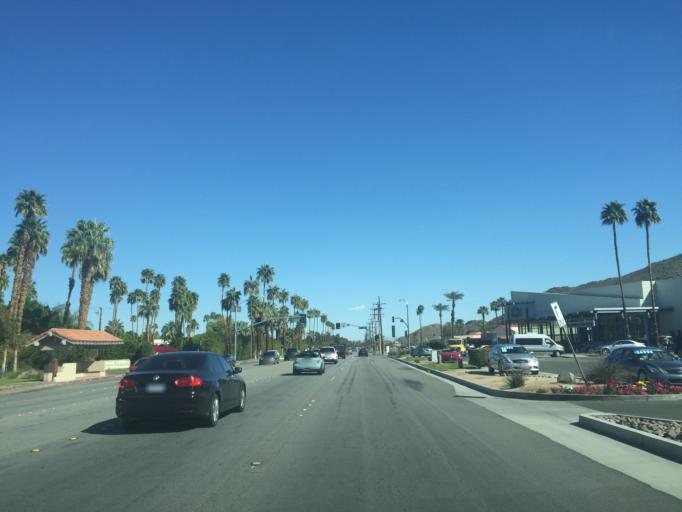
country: US
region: California
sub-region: Riverside County
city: Cathedral City
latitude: 33.7952
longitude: -116.5028
